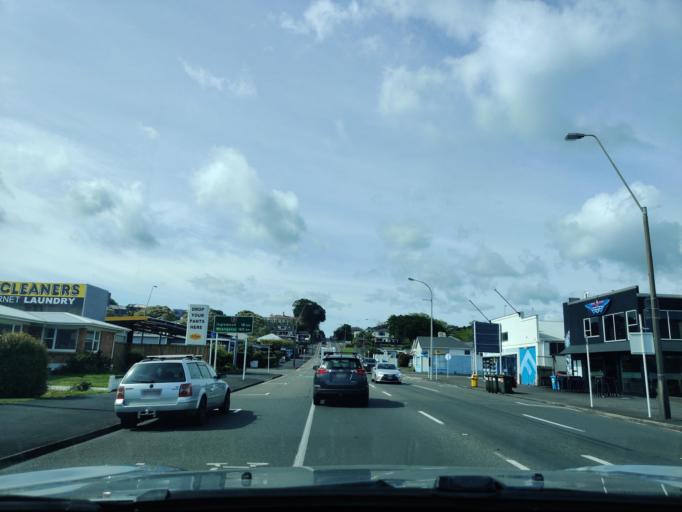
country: NZ
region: Taranaki
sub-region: New Plymouth District
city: New Plymouth
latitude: -39.0571
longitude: 174.0837
